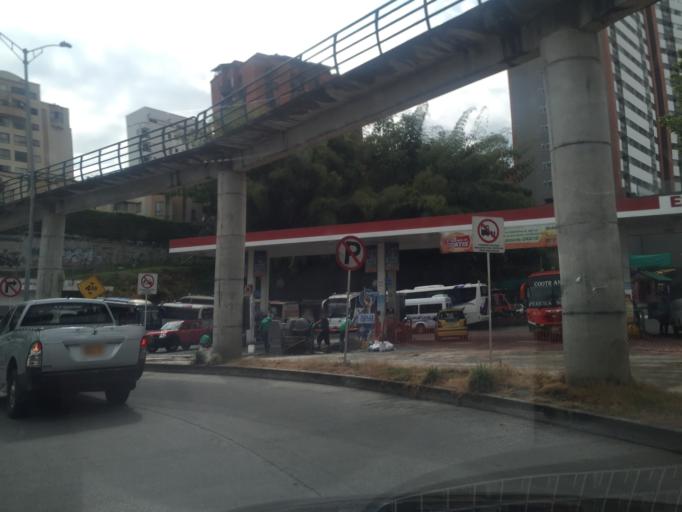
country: CO
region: Risaralda
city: Pereira
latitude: 4.8015
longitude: -75.6930
